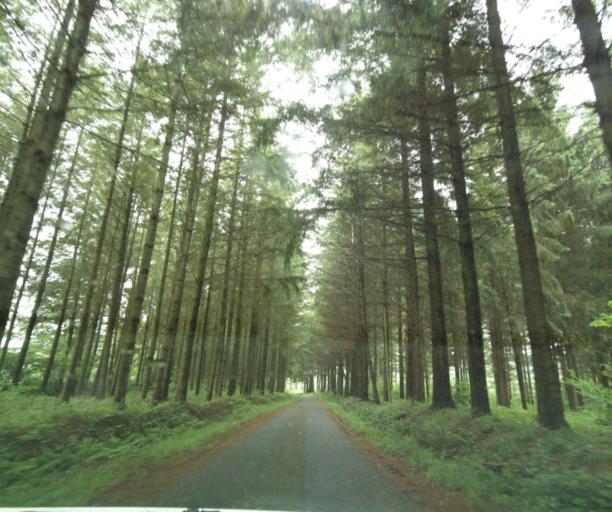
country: FR
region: Bourgogne
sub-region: Departement de Saone-et-Loire
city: Palinges
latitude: 46.5384
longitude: 4.2654
